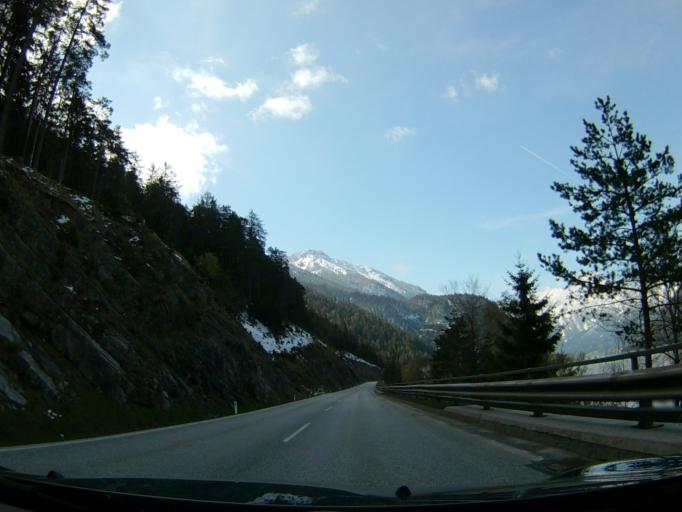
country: AT
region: Tyrol
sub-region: Politischer Bezirk Schwaz
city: Achenkirch
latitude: 47.4948
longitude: 11.7125
